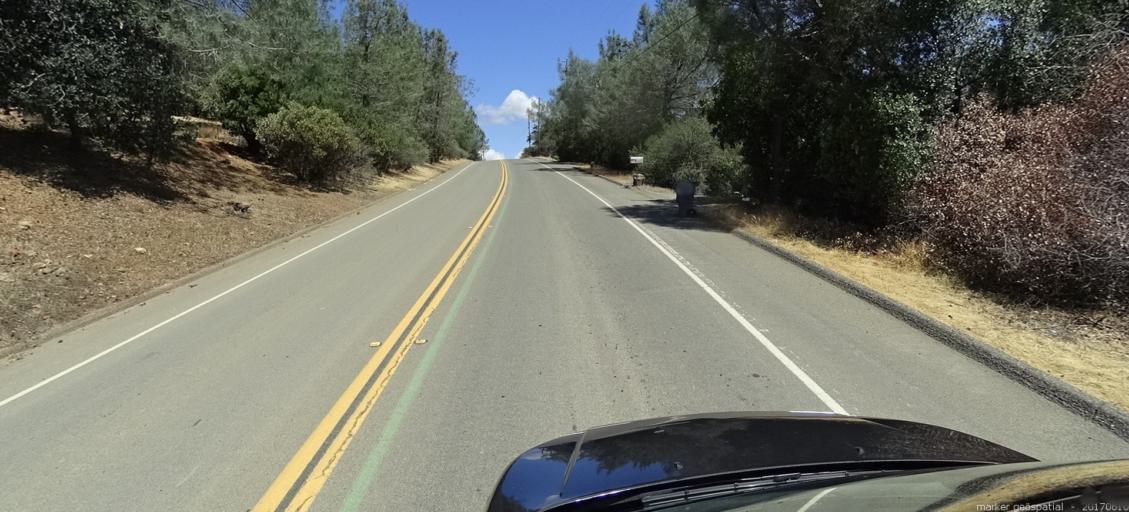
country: US
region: California
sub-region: Butte County
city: Oroville East
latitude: 39.5278
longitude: -121.4774
